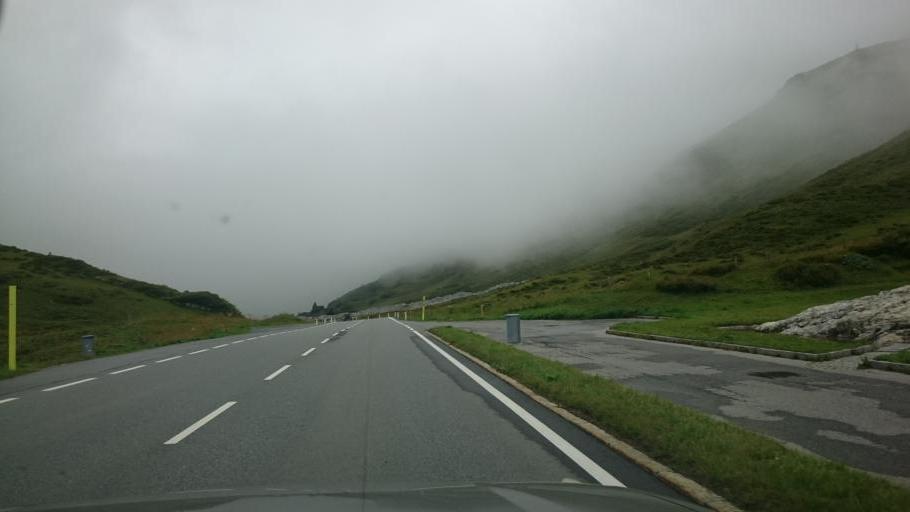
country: AT
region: Vorarlberg
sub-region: Politischer Bezirk Bludenz
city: Lech
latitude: 47.1578
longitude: 10.1647
